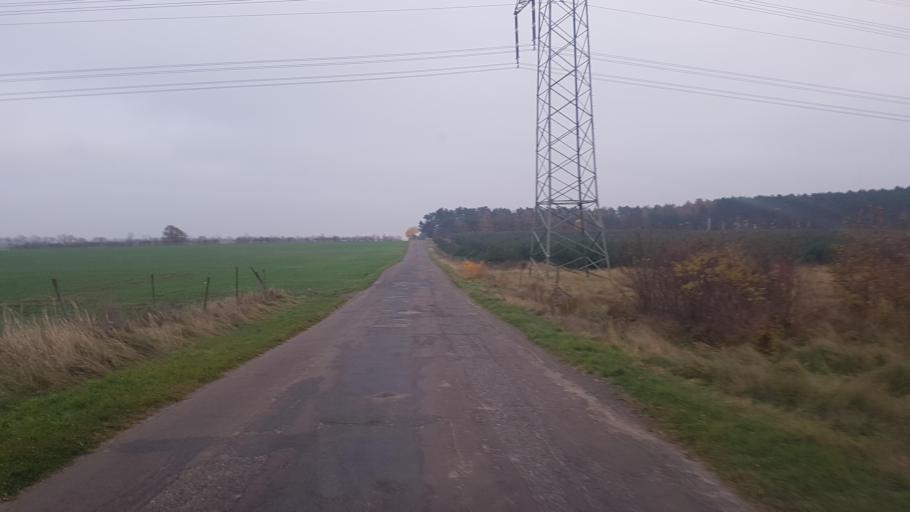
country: DE
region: Brandenburg
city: Gross Kreutz
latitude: 52.3767
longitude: 12.7975
